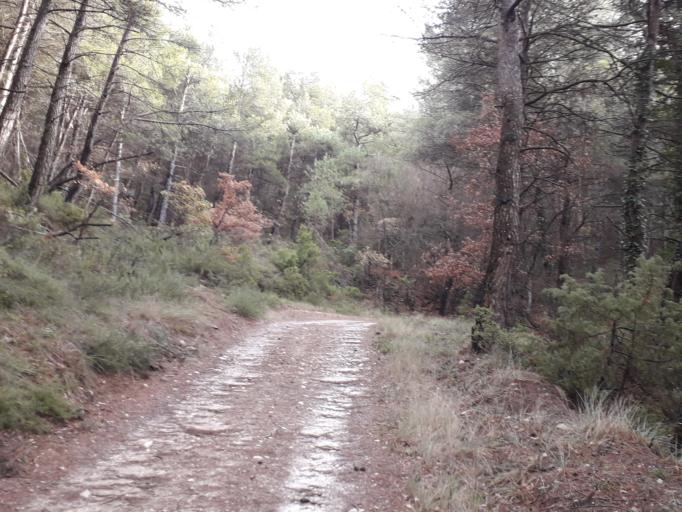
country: ES
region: Catalonia
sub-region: Provincia de Barcelona
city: Bellprat
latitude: 41.5363
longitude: 1.4382
